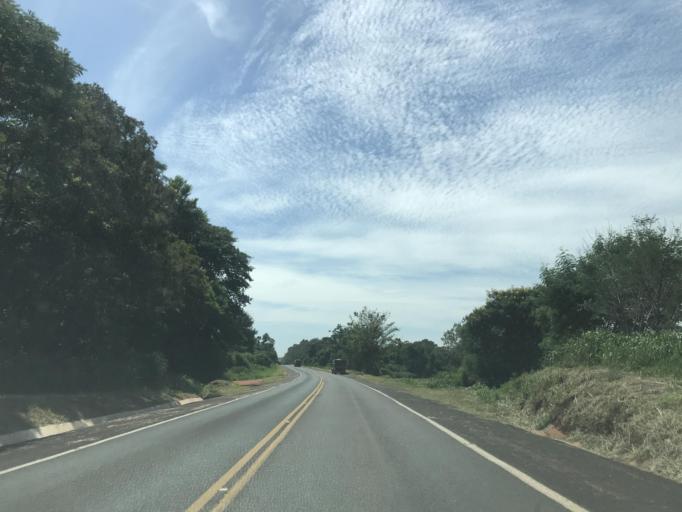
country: BR
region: Parana
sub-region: Paranavai
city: Nova Aurora
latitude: -22.9596
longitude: -52.6847
